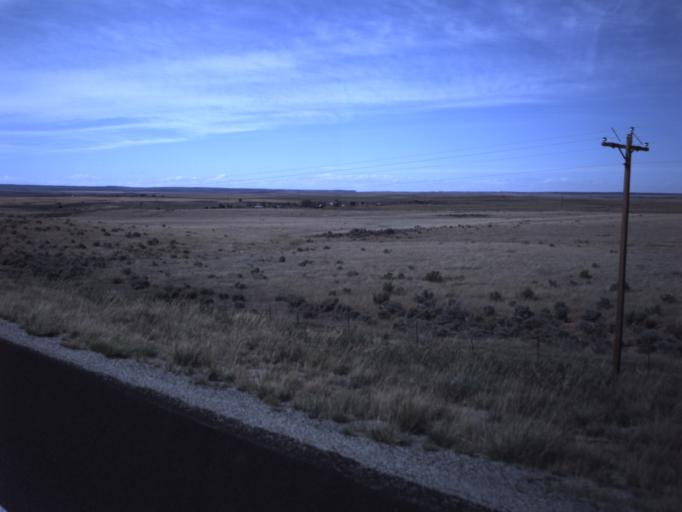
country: US
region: Utah
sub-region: San Juan County
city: Monticello
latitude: 37.8657
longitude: -109.2321
